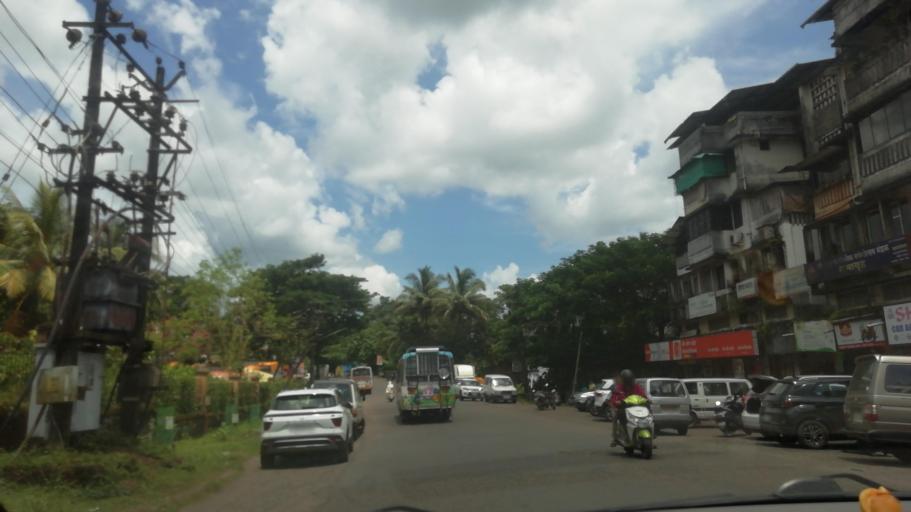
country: IN
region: Goa
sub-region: North Goa
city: Ponda
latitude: 15.4027
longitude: 74.0031
